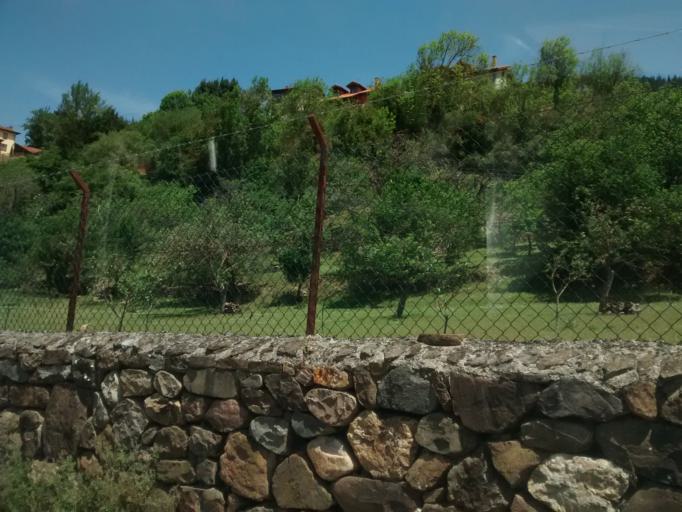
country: ES
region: Cantabria
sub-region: Provincia de Cantabria
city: Potes
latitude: 43.1769
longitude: -4.6000
